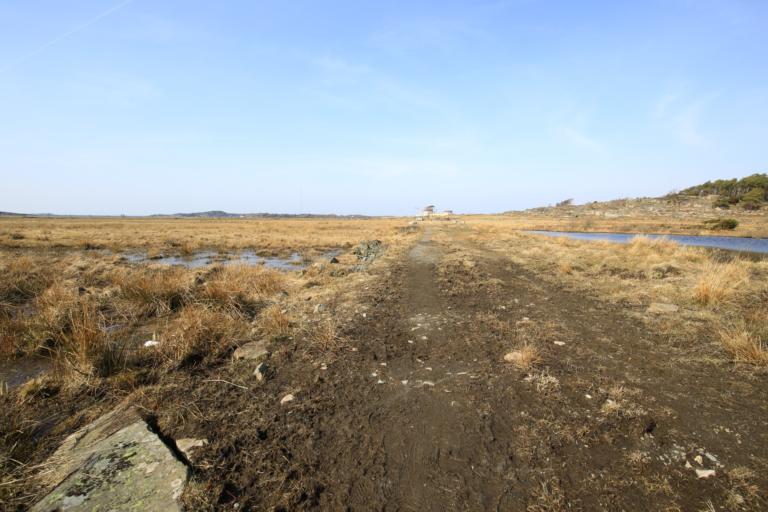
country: SE
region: Halland
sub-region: Kungsbacka Kommun
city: Frillesas
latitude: 57.2508
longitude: 12.1309
